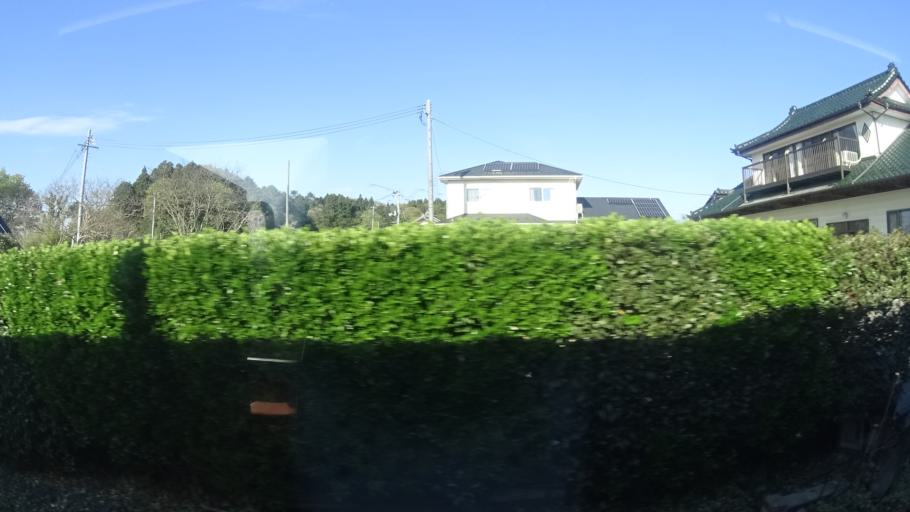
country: JP
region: Fukushima
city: Namie
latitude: 37.5976
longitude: 140.9968
